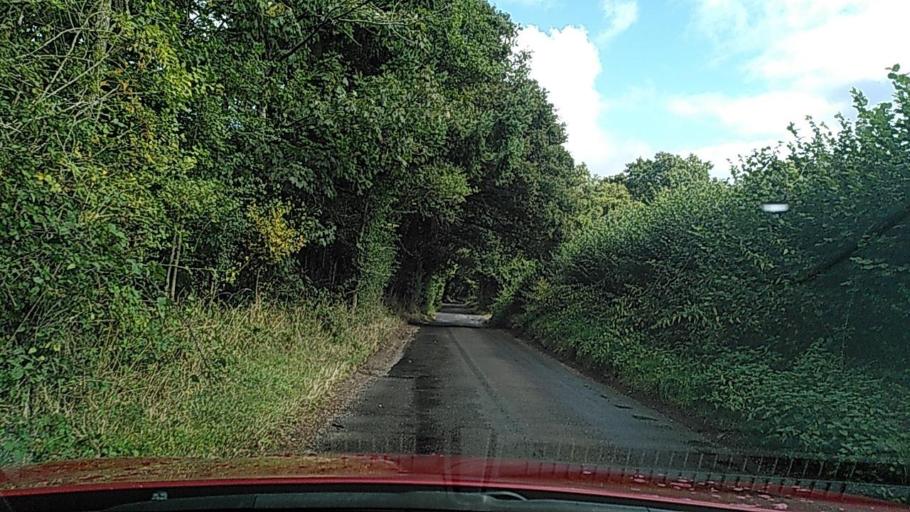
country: GB
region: England
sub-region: Oxfordshire
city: Henley on Thames
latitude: 51.5097
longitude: -0.9247
